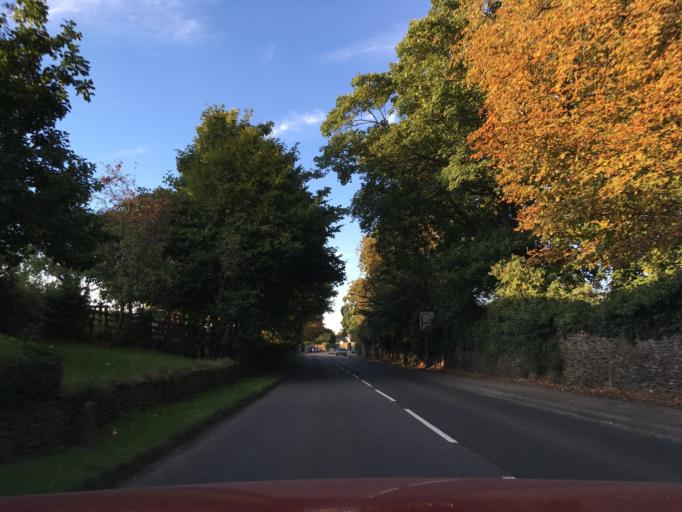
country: GB
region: England
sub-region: South Gloucestershire
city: Winterbourne
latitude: 51.5073
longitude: -2.5190
